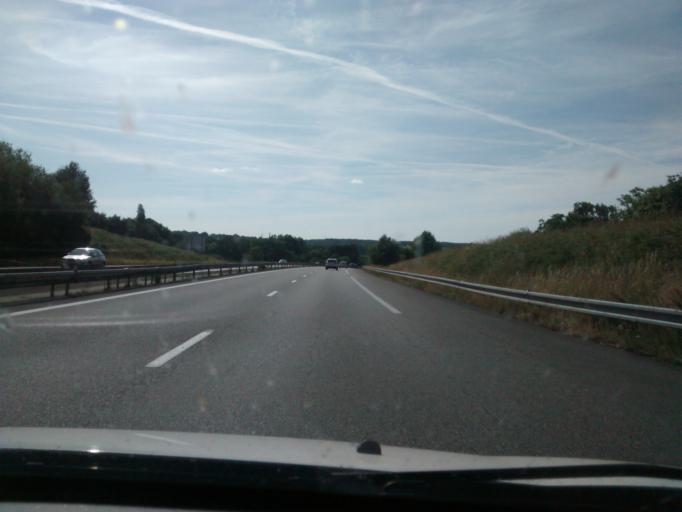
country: FR
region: Pays de la Loire
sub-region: Departement de la Mayenne
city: Port-Brillet
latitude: 48.0776
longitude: -0.9935
